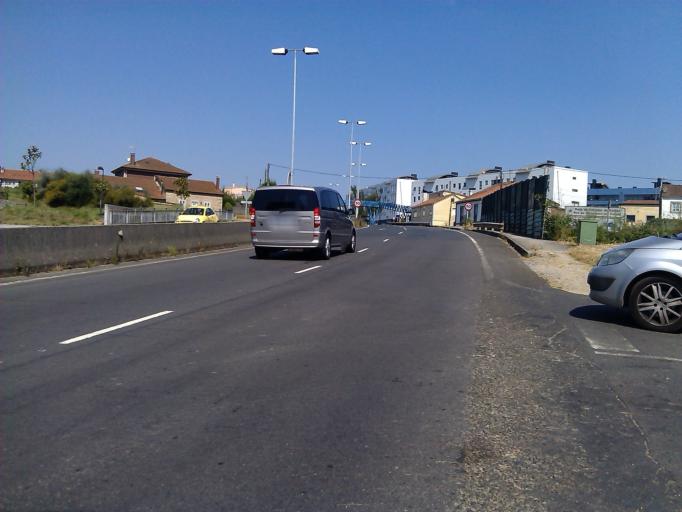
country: ES
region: Galicia
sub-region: Provincia da Coruna
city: Santiago de Compostela
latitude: 42.8572
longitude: -8.5331
